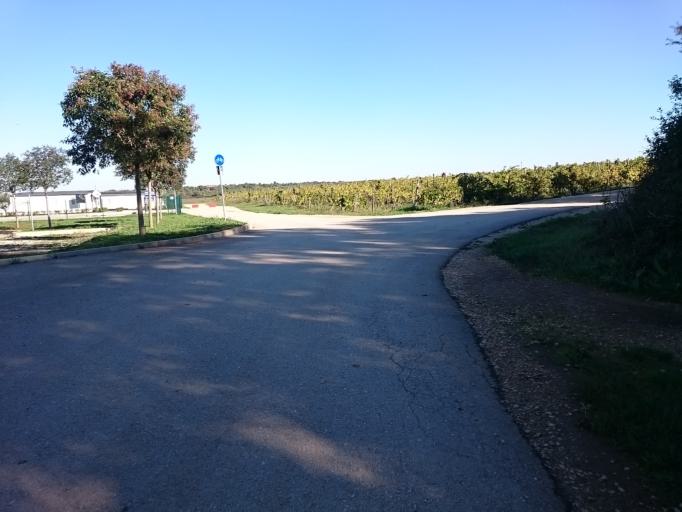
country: HR
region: Istarska
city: Novigrad
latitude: 45.3299
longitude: 13.5441
